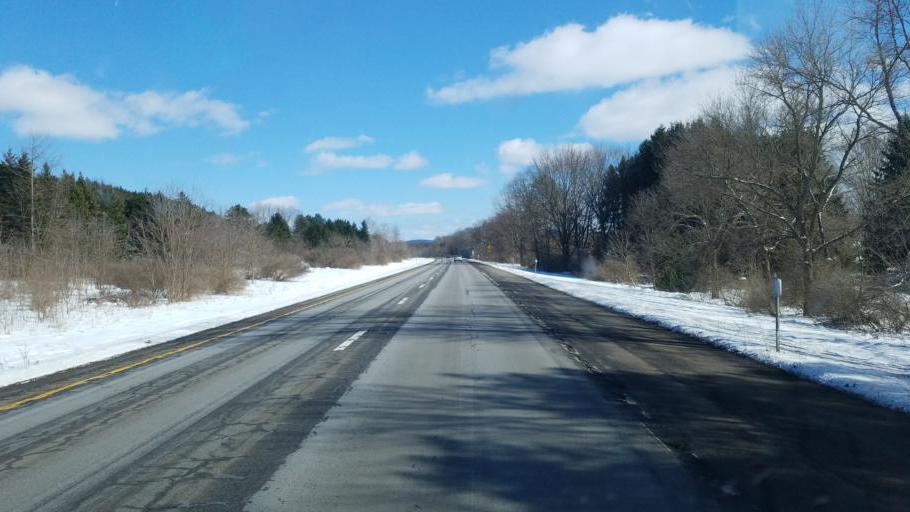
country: US
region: New York
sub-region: Chautauqua County
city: Falconer
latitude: 42.1352
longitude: -79.1499
